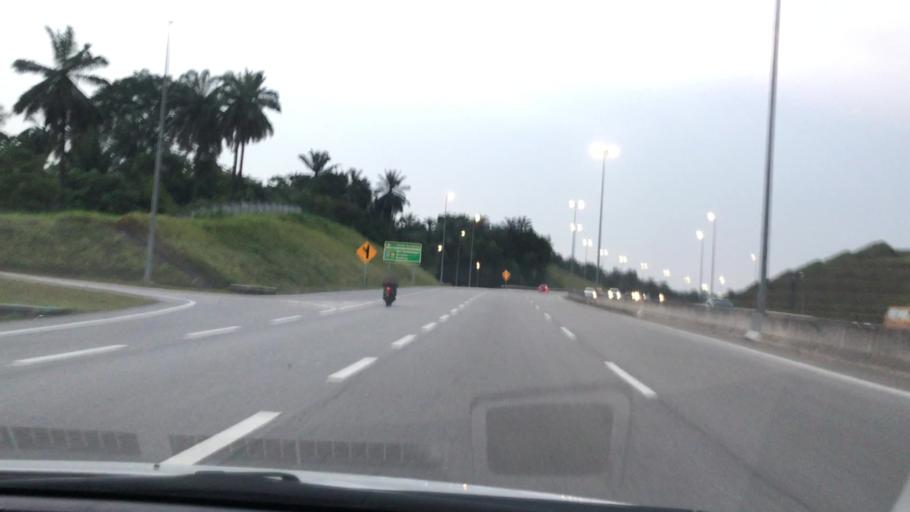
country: MY
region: Putrajaya
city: Putrajaya
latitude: 3.0027
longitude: 101.6877
